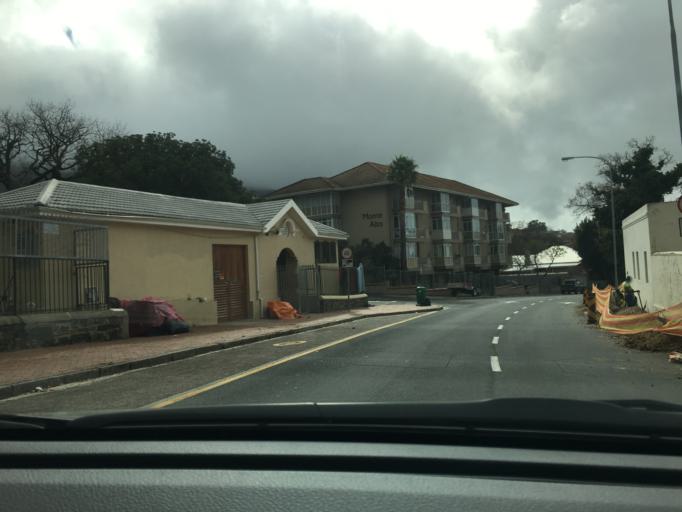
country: ZA
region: Western Cape
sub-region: City of Cape Town
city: Cape Town
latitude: -33.9295
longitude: 18.4079
